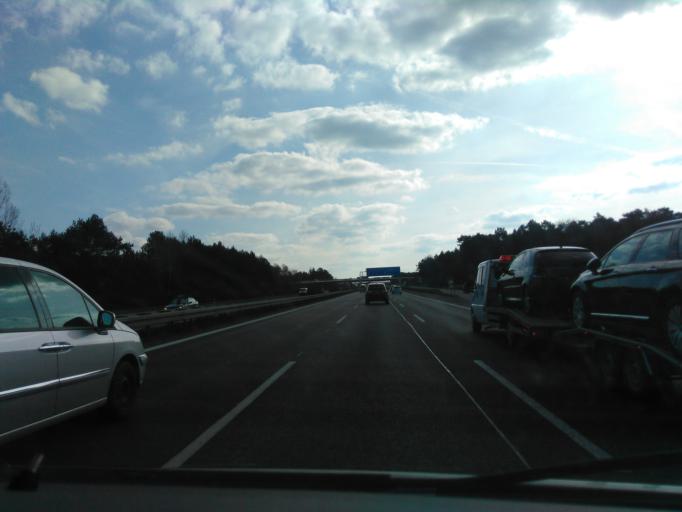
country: DE
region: Brandenburg
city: Schulzendorf
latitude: 52.3260
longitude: 13.5540
